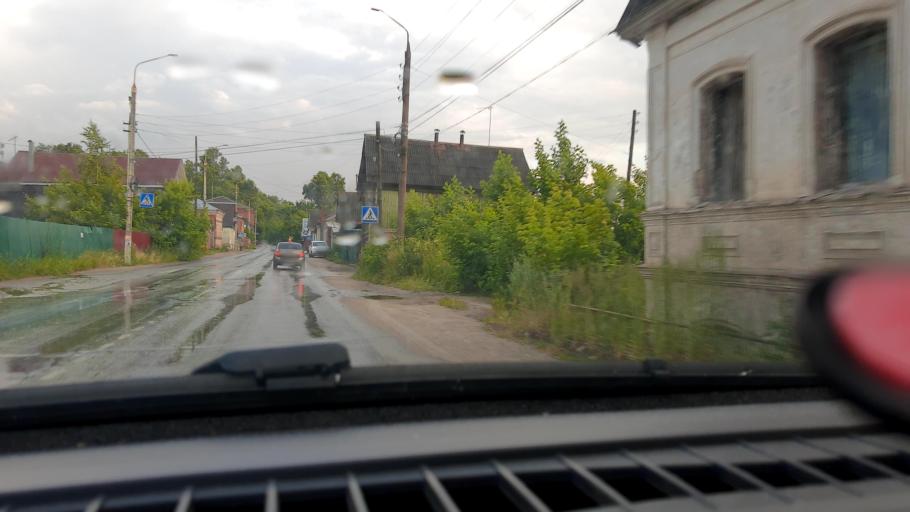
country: RU
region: Nizjnij Novgorod
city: Gorodets
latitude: 56.6521
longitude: 43.4649
